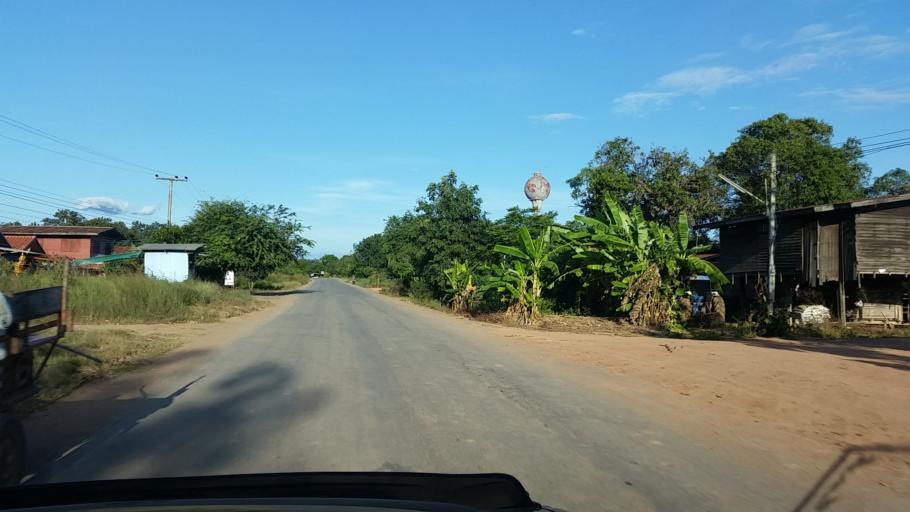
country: TH
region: Chaiyaphum
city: Thep Sathit
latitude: 15.5440
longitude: 101.4812
